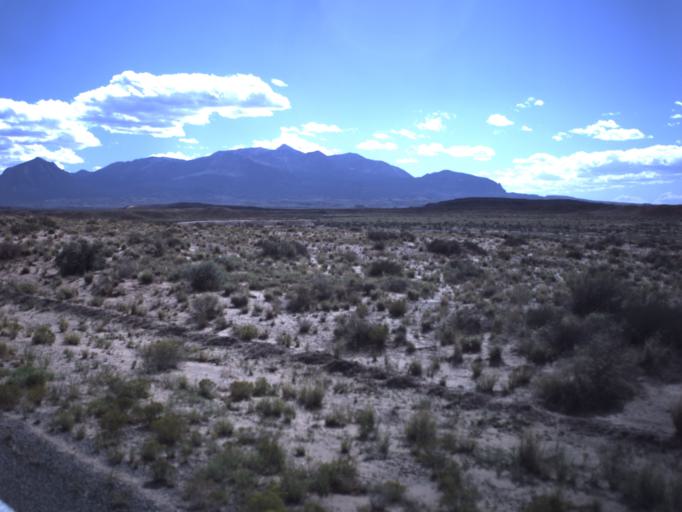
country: US
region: Utah
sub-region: Emery County
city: Ferron
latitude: 38.3174
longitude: -110.6740
